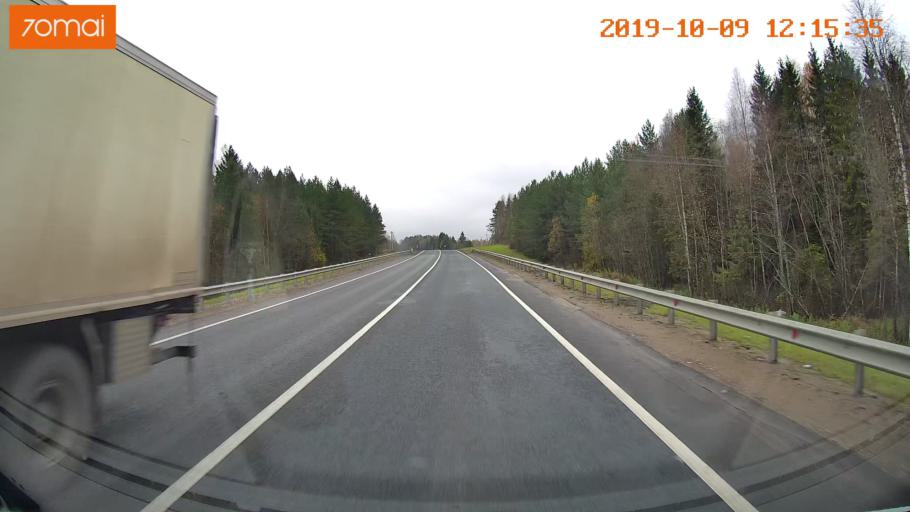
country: RU
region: Jaroslavl
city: Prechistoye
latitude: 58.4812
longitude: 40.3233
